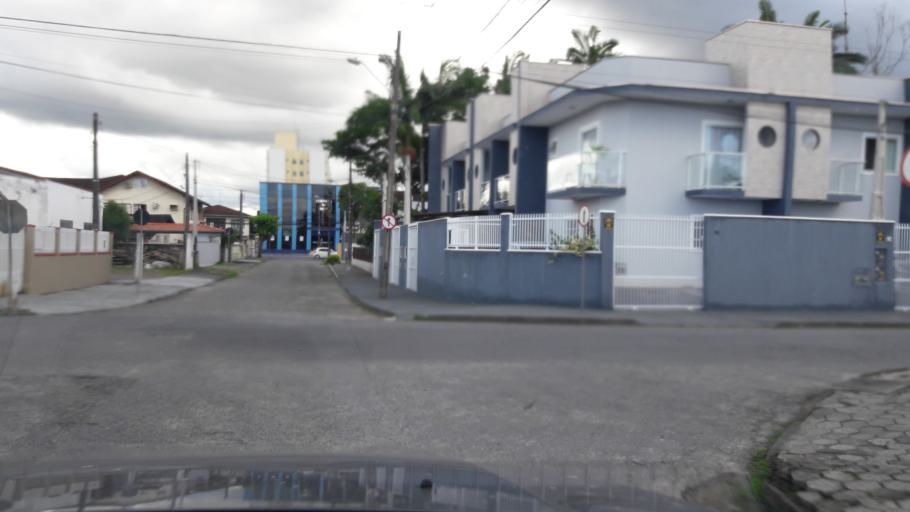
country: BR
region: Santa Catarina
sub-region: Joinville
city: Joinville
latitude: -26.3246
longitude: -48.8357
